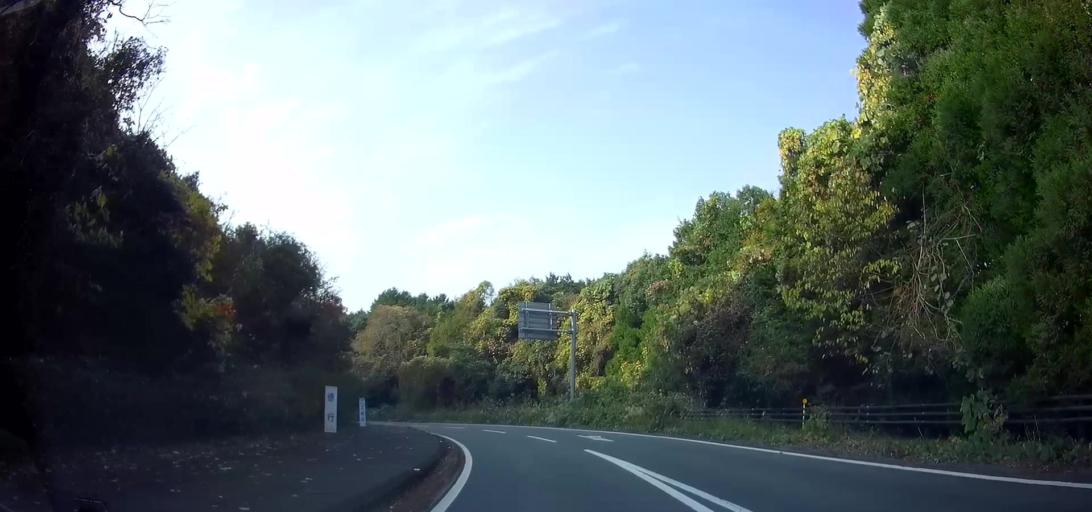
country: JP
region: Nagasaki
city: Shimabara
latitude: 32.6863
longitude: 130.2027
